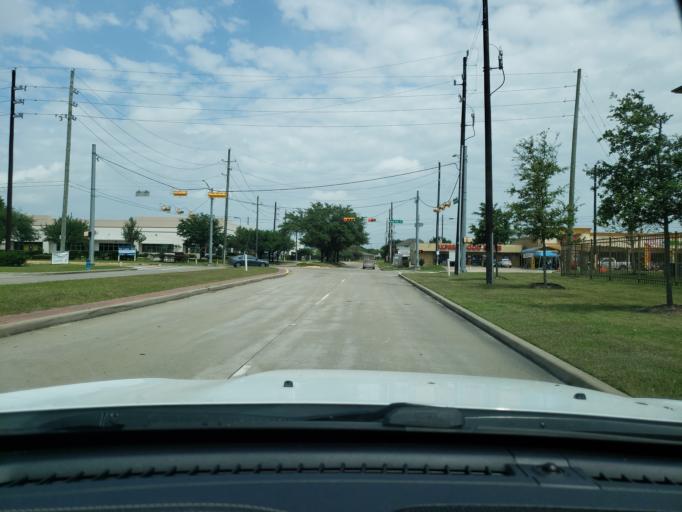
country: US
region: Texas
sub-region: Fort Bend County
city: Cinco Ranch
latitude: 29.7891
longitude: -95.7309
